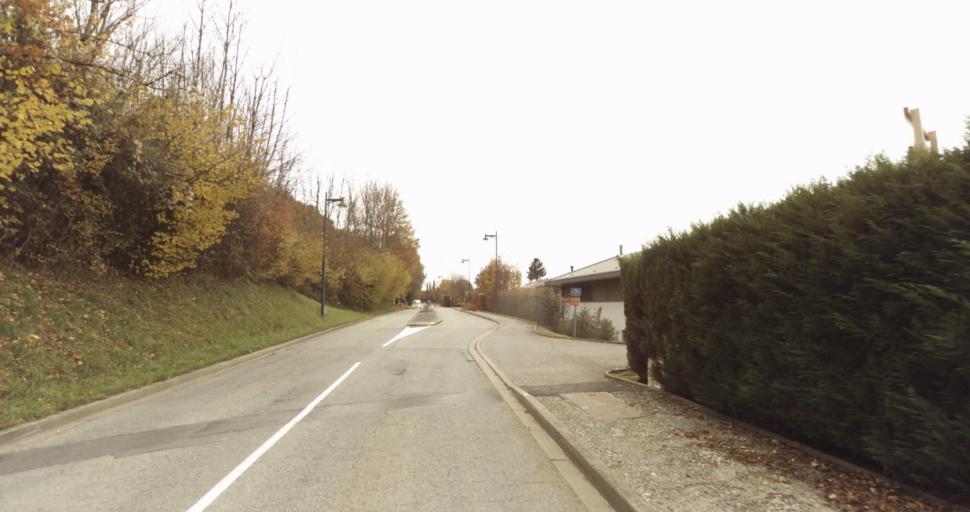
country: FR
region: Rhone-Alpes
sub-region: Departement de la Haute-Savoie
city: Annecy-le-Vieux
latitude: 45.9321
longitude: 6.1428
